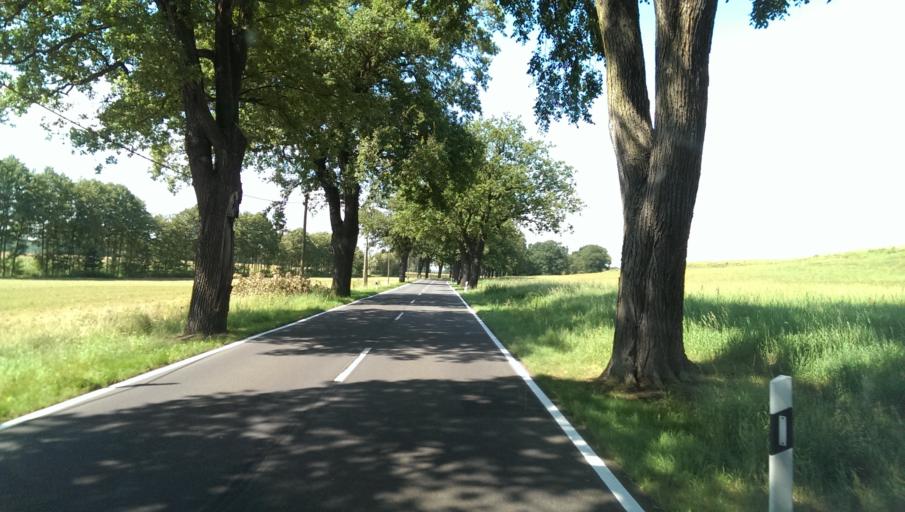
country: DE
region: Brandenburg
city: Trebbin
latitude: 52.2413
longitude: 13.2212
